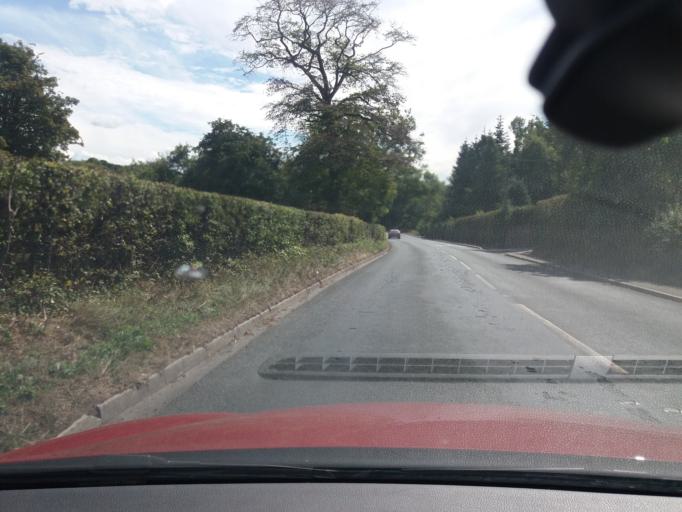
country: GB
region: England
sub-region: Lancashire
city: Euxton
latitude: 53.6629
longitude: -2.7080
